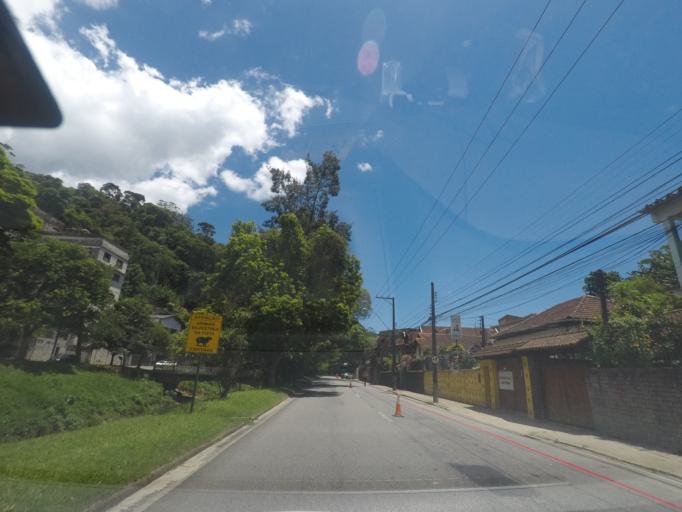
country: BR
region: Rio de Janeiro
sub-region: Petropolis
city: Petropolis
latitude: -22.4942
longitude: -43.1795
